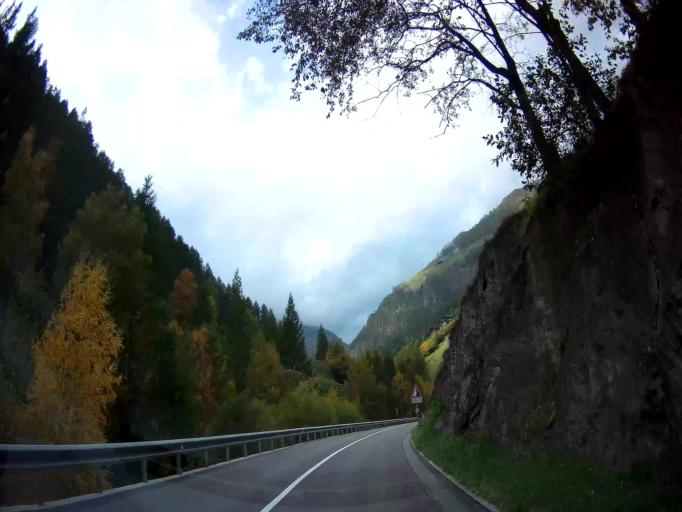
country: IT
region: Trentino-Alto Adige
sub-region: Bolzano
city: Senales
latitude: 46.7119
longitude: 10.8955
